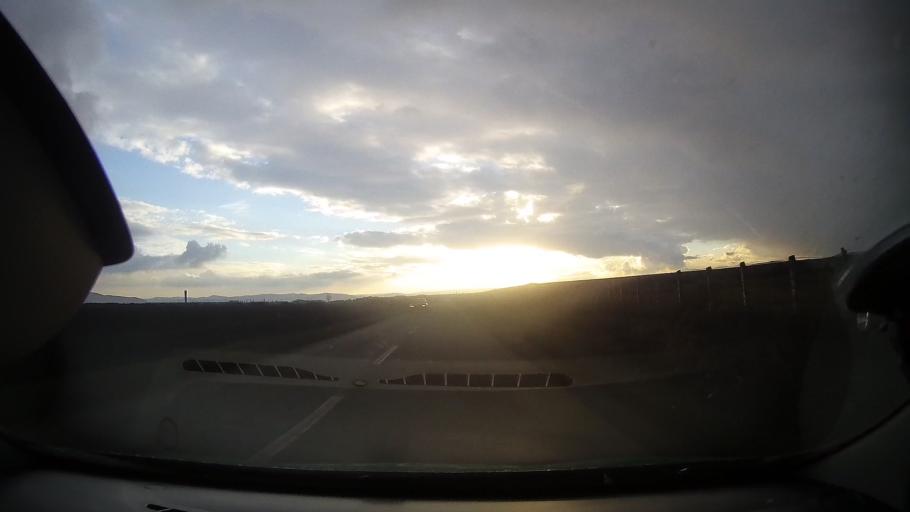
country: RO
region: Alba
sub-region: Comuna Lunca Muresului
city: Lunca Muresului
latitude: 46.4472
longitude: 23.9167
